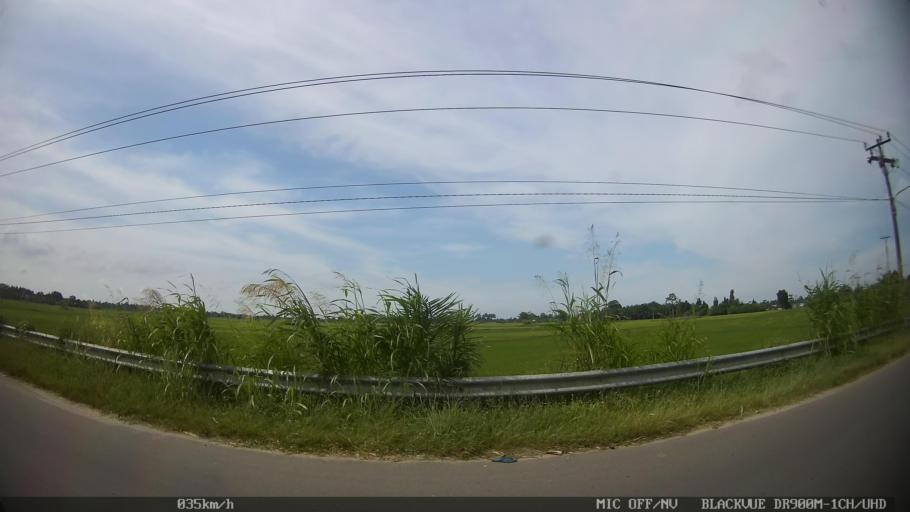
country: ID
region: North Sumatra
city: Percut
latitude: 3.6154
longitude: 98.8403
